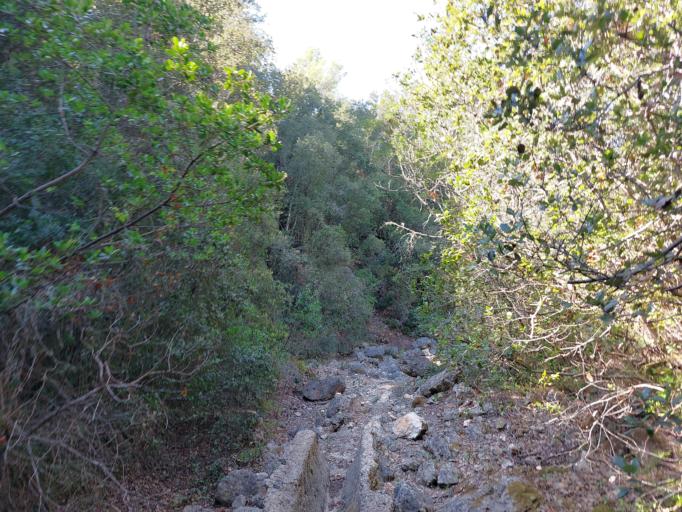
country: HR
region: Dubrovacko-Neretvanska
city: Smokvica
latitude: 42.7405
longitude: 16.8245
